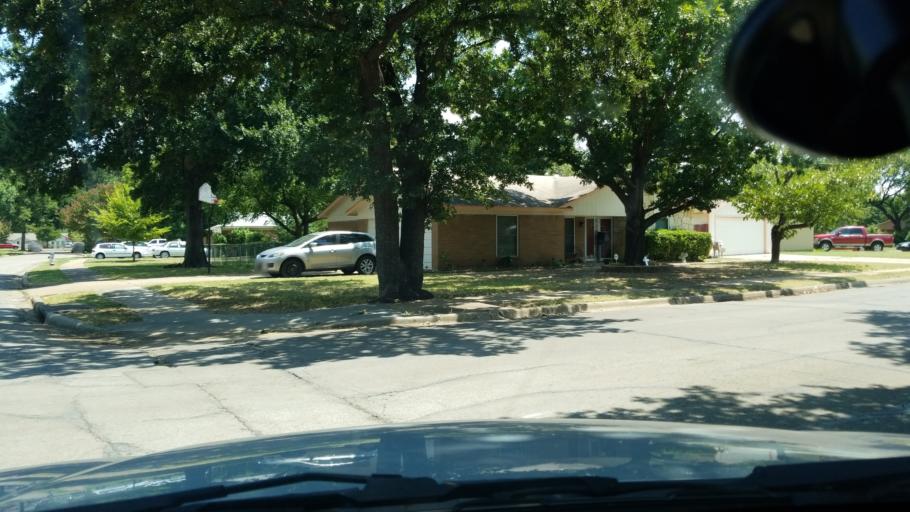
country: US
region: Texas
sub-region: Dallas County
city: Irving
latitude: 32.8240
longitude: -96.9903
